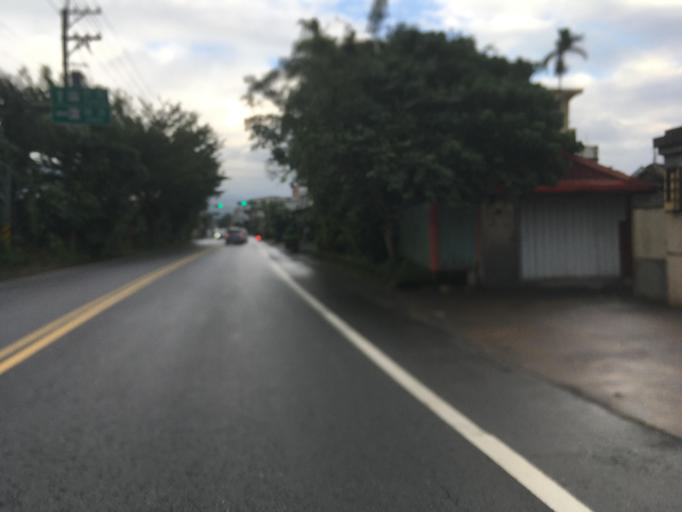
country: TW
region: Taiwan
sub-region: Yilan
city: Yilan
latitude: 24.8340
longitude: 121.8034
